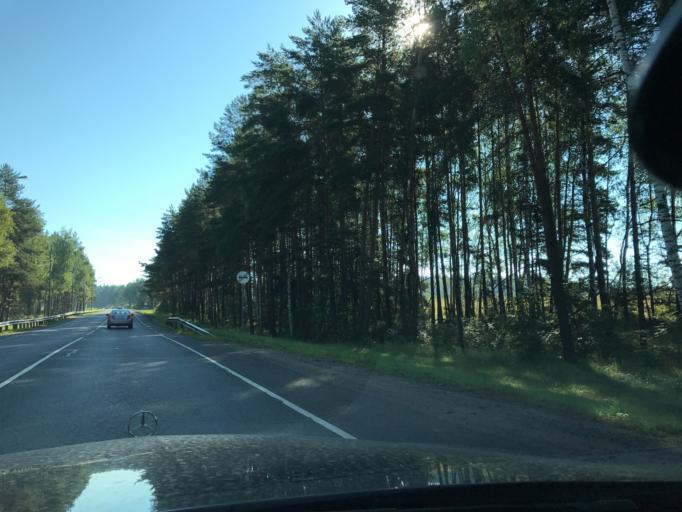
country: RU
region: Moskovskaya
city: Chernogolovka
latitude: 55.9622
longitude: 38.2699
